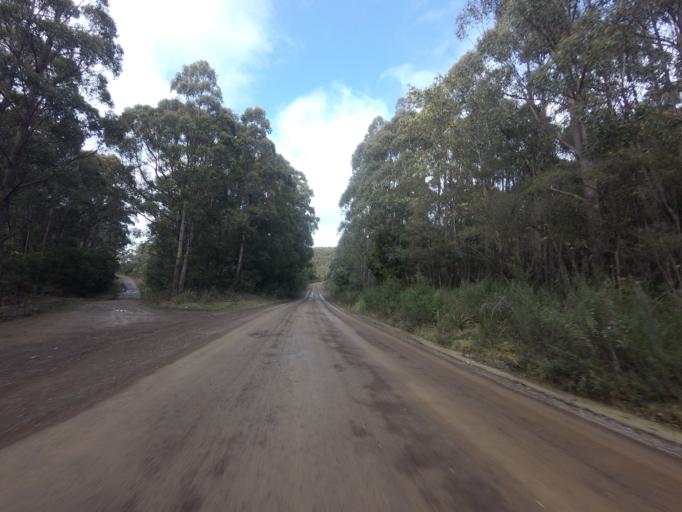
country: AU
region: Tasmania
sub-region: Huon Valley
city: Geeveston
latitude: -43.4653
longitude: 146.8999
